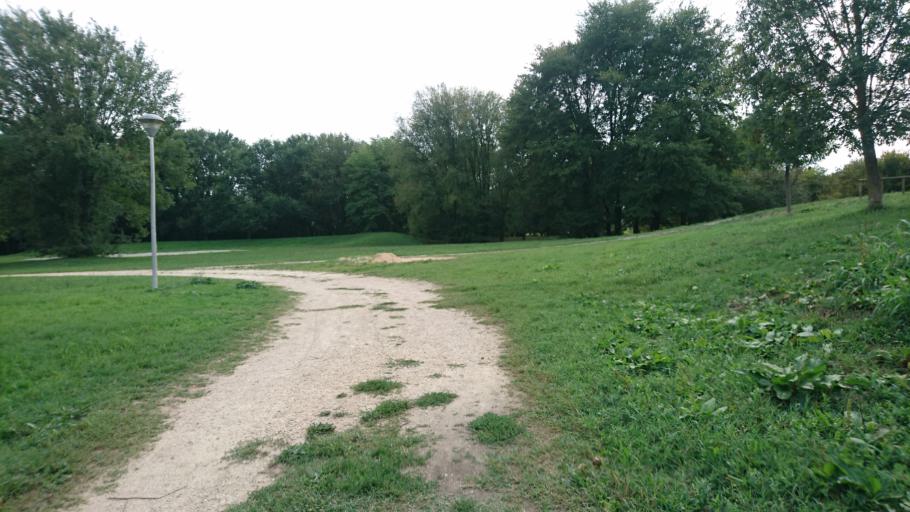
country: IT
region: Veneto
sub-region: Provincia di Padova
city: Villaguattera
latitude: 45.4365
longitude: 11.8456
